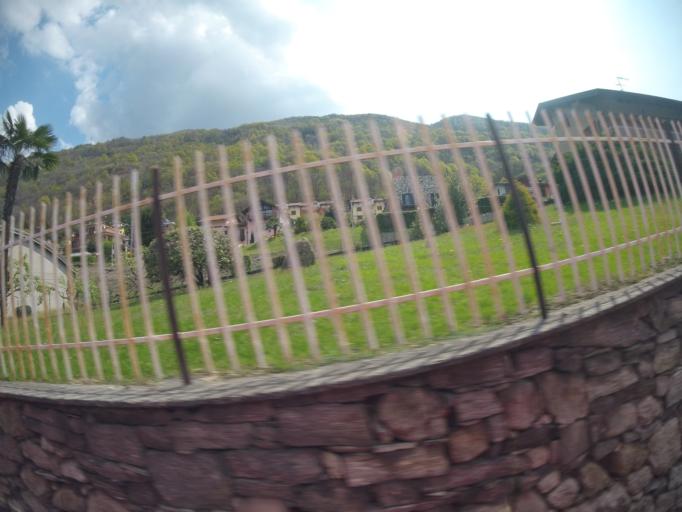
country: IT
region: Piedmont
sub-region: Provincia Verbano-Cusio-Ossola
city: Omegna
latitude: 45.8630
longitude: 8.4125
